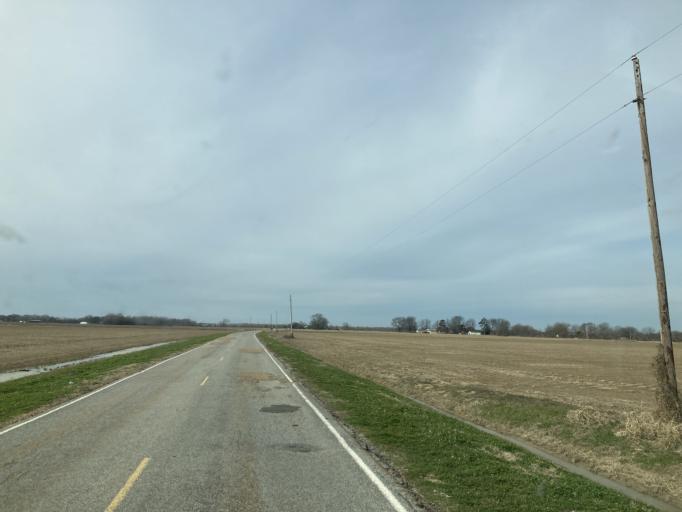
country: US
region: Mississippi
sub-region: Humphreys County
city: Belzoni
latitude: 33.0566
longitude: -90.6539
